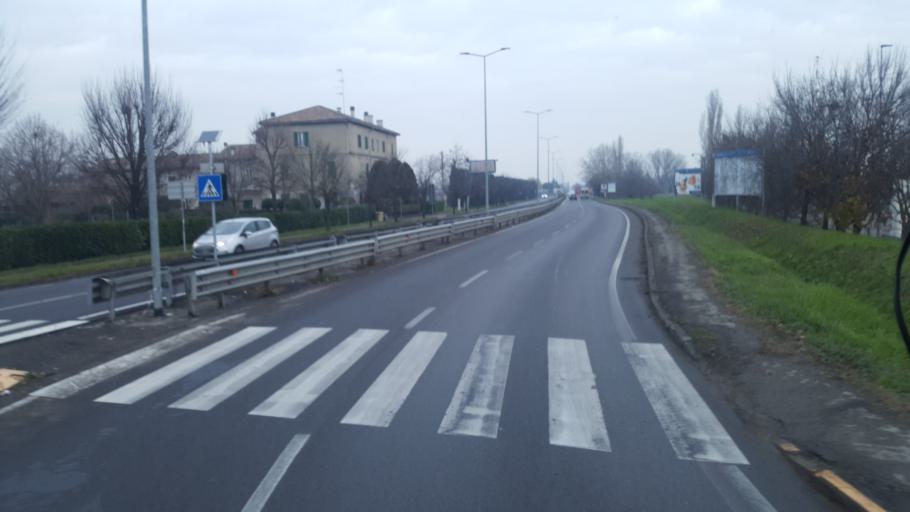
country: IT
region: Emilia-Romagna
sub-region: Provincia di Parma
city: Parma
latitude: 44.8270
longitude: 10.3294
